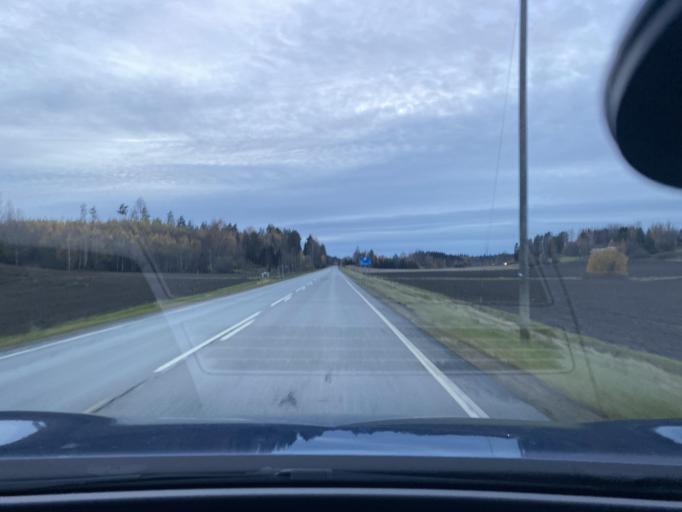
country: FI
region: Uusimaa
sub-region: Helsinki
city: Saukkola
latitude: 60.3855
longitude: 23.8999
